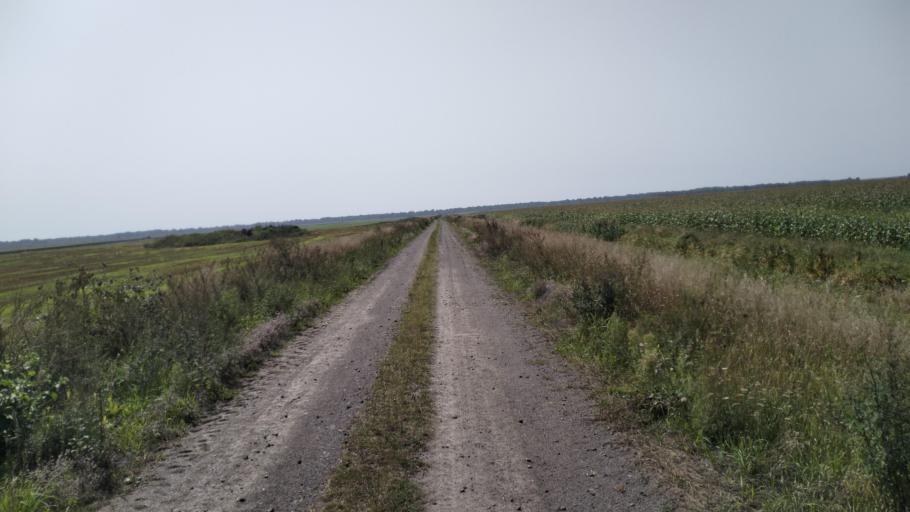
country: BY
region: Brest
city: Davyd-Haradok
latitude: 51.9901
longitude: 27.1643
